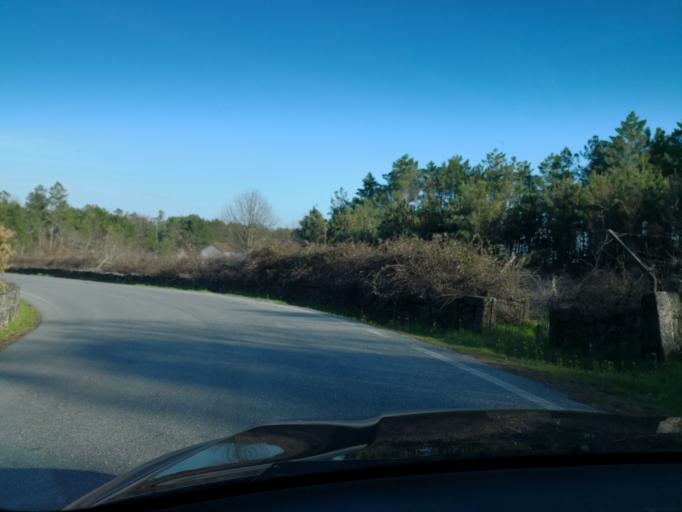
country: PT
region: Vila Real
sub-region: Sabrosa
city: Sabrosa
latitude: 41.3511
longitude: -7.6061
